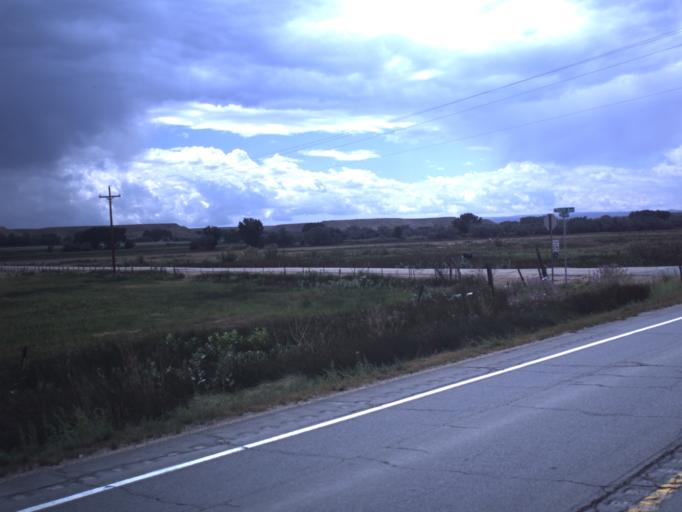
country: US
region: Utah
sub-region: Duchesne County
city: Roosevelt
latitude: 40.1609
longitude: -110.1660
